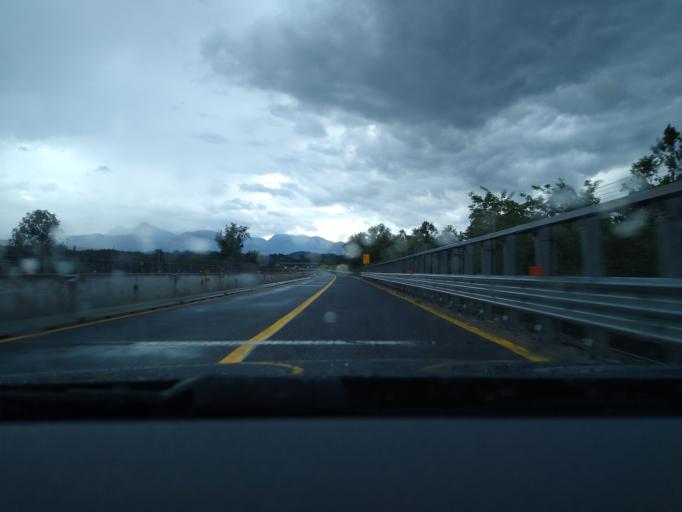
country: IT
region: Friuli Venezia Giulia
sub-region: Provincia di Udine
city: Cassacco
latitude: 46.1549
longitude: 13.1693
